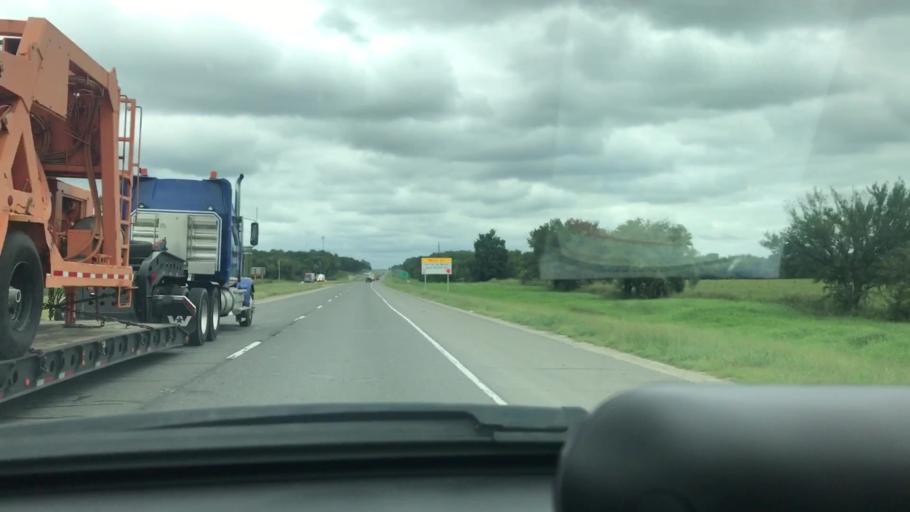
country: US
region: Oklahoma
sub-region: Muskogee County
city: Muskogee
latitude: 35.8140
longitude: -95.4024
